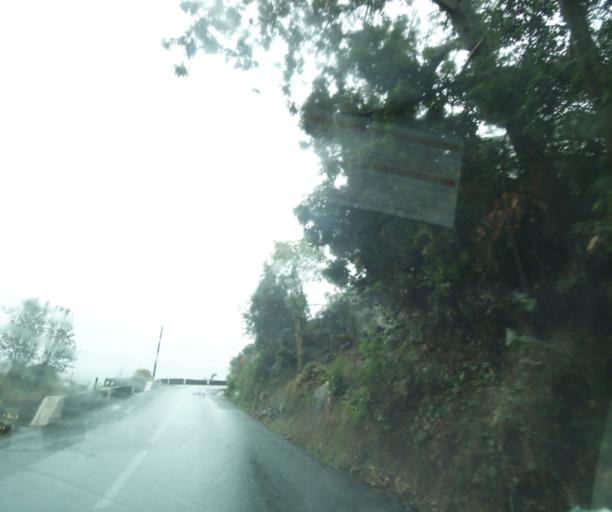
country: RE
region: Reunion
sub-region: Reunion
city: Saint-Paul
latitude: -21.0194
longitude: 55.3016
